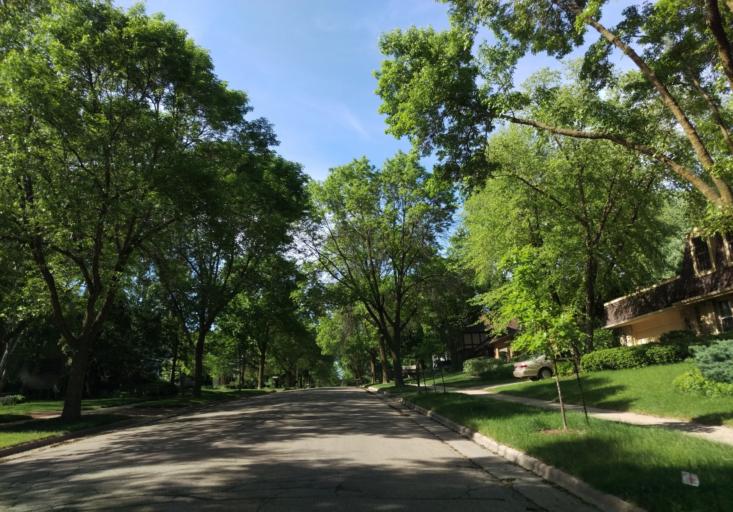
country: US
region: Wisconsin
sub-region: Dane County
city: Middleton
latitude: 43.0697
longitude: -89.4990
